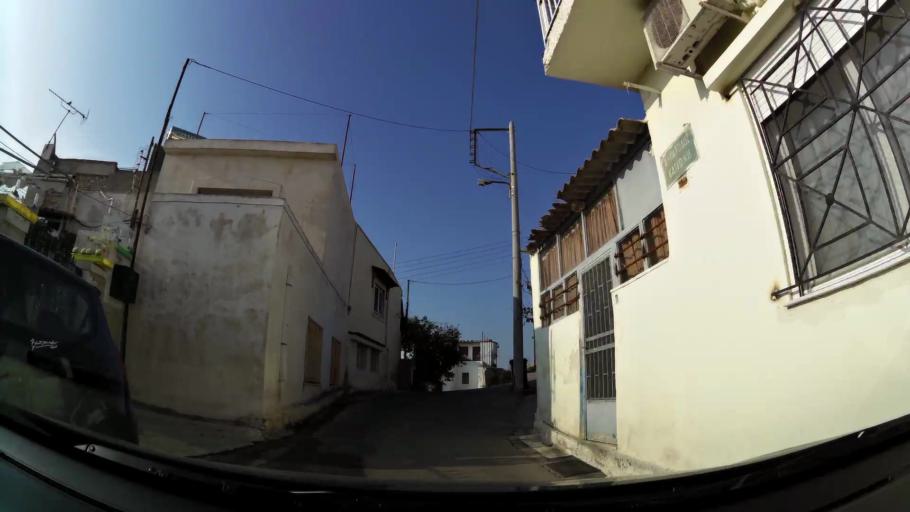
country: GR
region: Attica
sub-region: Nomos Piraios
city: Keratsini
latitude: 37.9666
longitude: 23.6323
